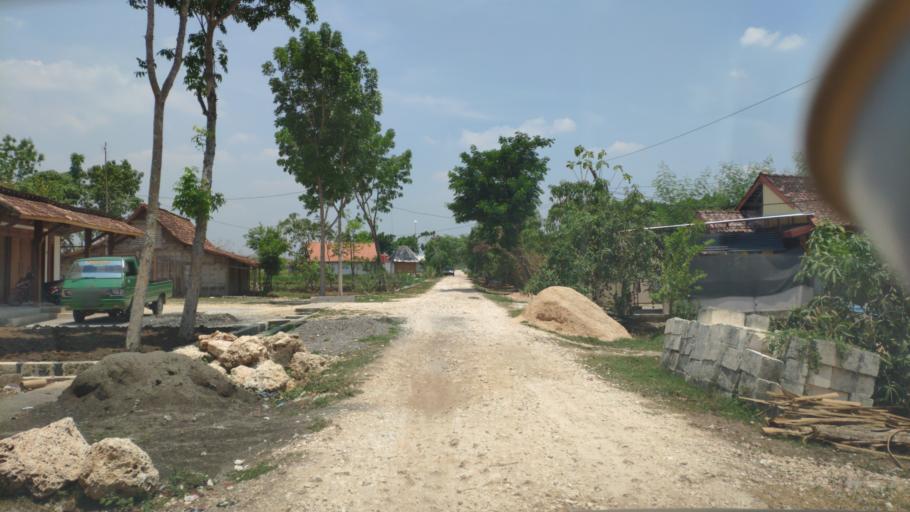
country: ID
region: Central Java
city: Gesik
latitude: -7.0441
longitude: 111.3275
